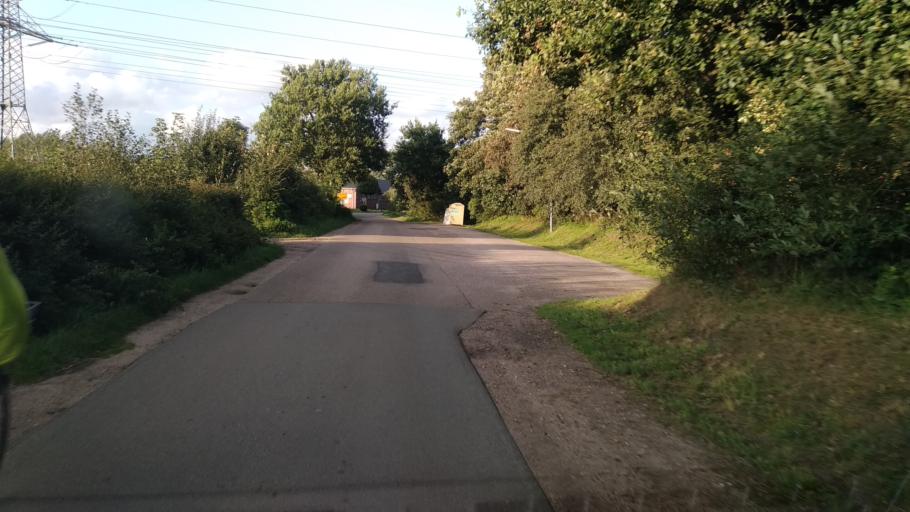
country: DE
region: Schleswig-Holstein
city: Klein Bennebek
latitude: 54.4033
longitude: 9.4590
